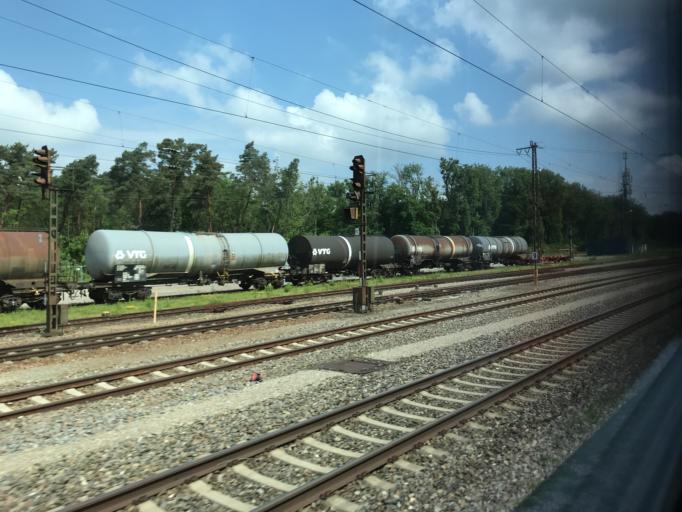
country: DE
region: Bavaria
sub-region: Swabia
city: Offingen
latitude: 48.4839
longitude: 10.3472
